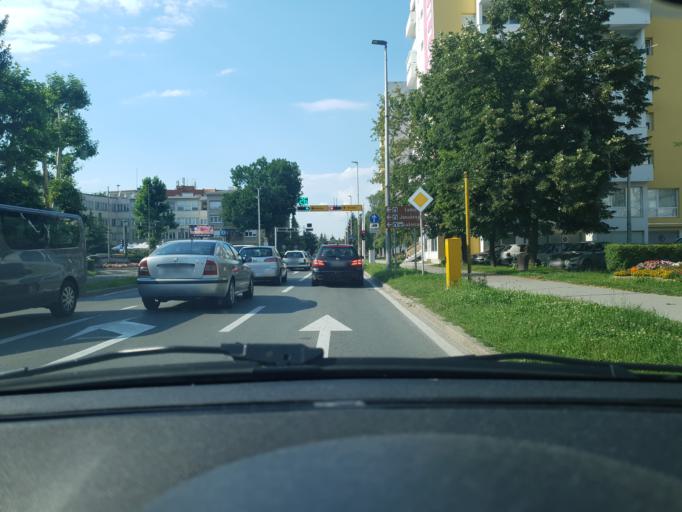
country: HR
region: Zagrebacka
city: Zapresic
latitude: 45.8567
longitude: 15.8053
